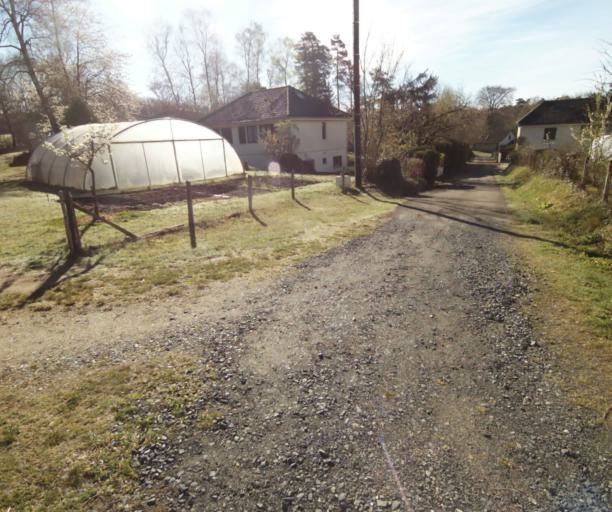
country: FR
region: Limousin
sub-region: Departement de la Correze
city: Correze
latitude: 45.2698
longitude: 1.8859
